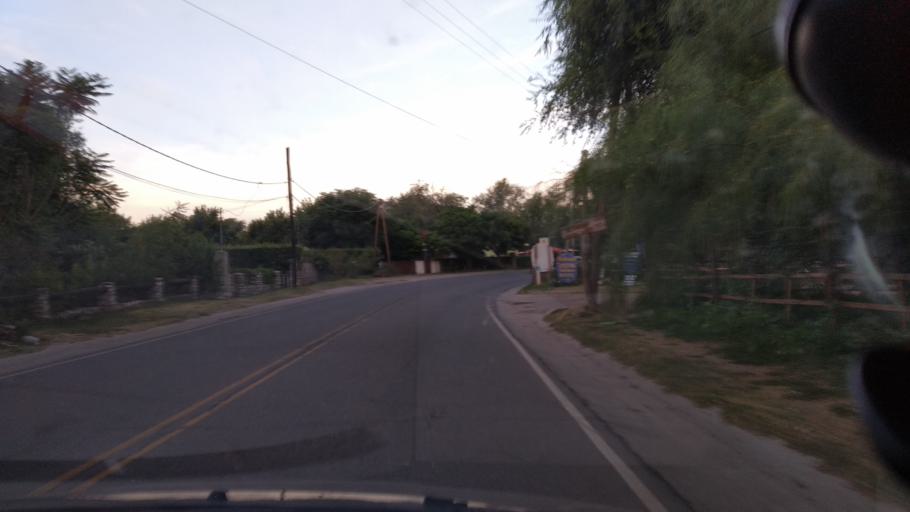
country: AR
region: Cordoba
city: Villa Las Rosas
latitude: -31.9524
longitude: -65.0591
